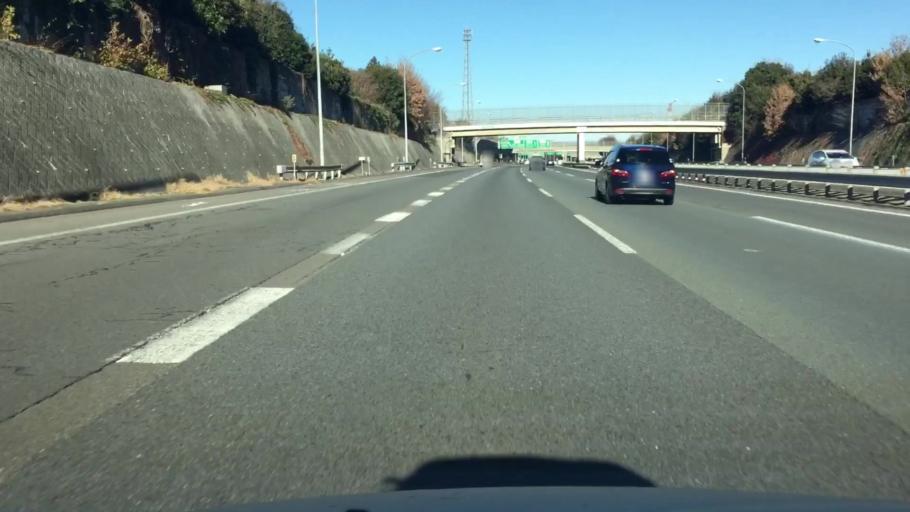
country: JP
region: Saitama
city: Sakado
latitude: 35.9259
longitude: 139.4108
